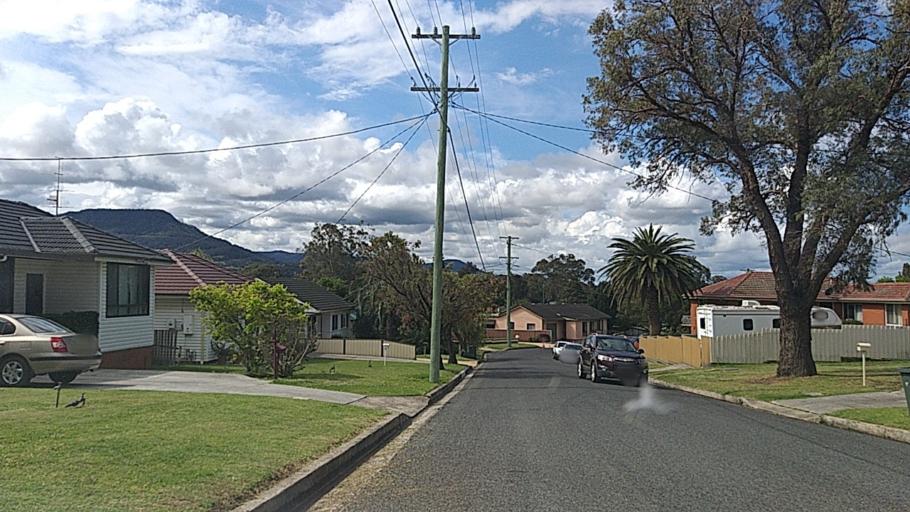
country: AU
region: New South Wales
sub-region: Wollongong
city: Koonawarra
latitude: -34.4925
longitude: 150.8043
